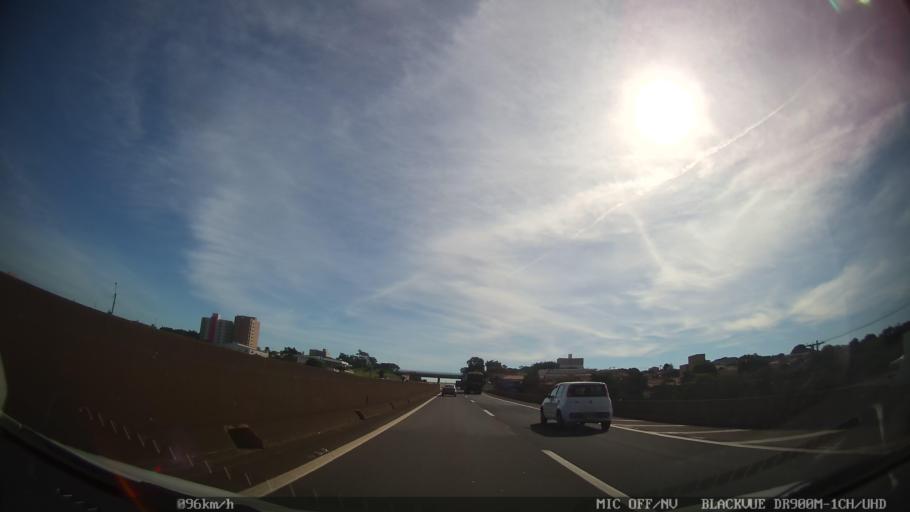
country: BR
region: Sao Paulo
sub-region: Araras
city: Araras
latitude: -22.3604
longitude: -47.3946
